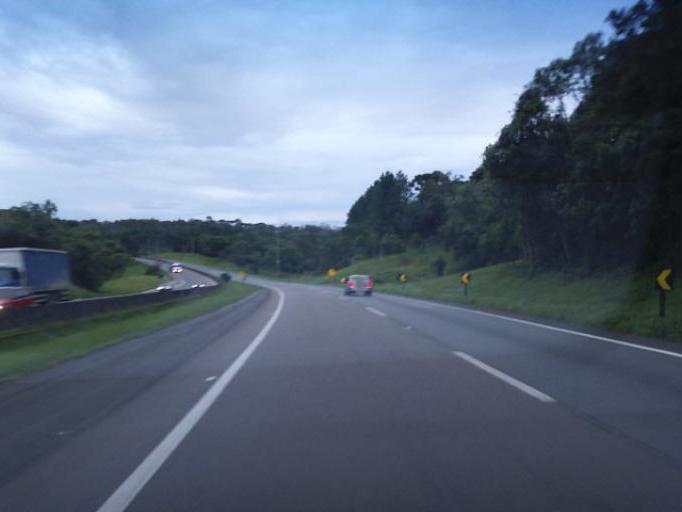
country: BR
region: Parana
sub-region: Sao Jose Dos Pinhais
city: Sao Jose dos Pinhais
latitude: -25.8031
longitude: -49.1348
